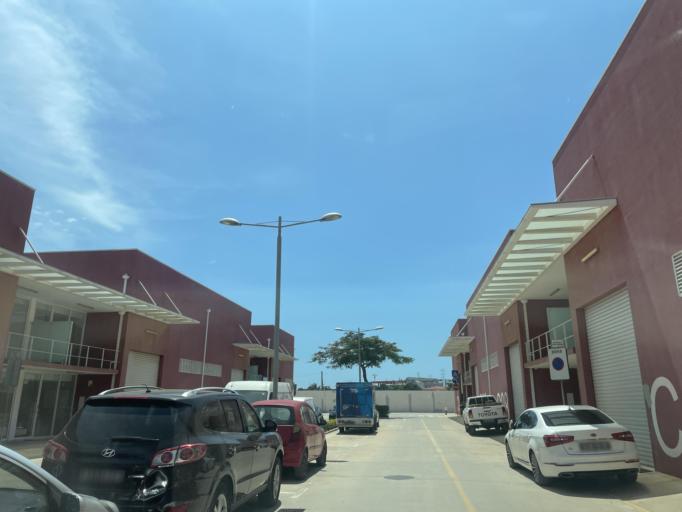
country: AO
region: Luanda
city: Luanda
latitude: -8.9093
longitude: 13.2065
